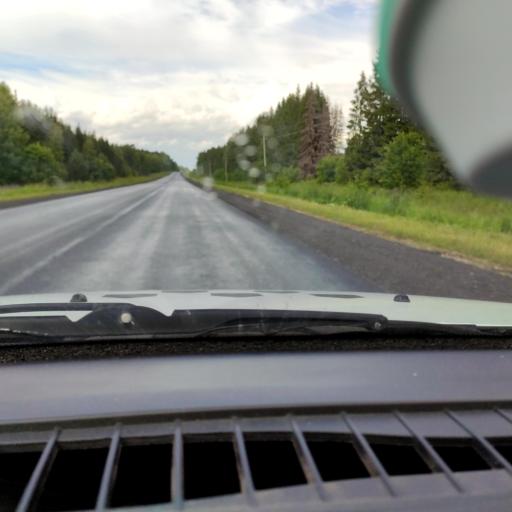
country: RU
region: Perm
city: Orda
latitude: 57.2191
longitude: 56.9480
